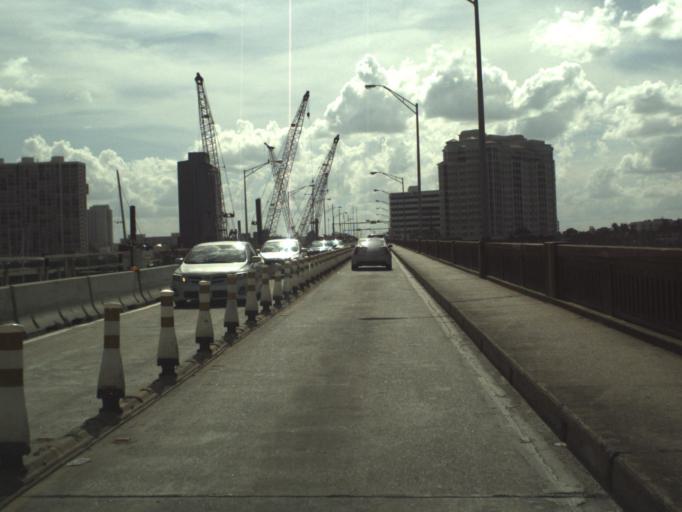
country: US
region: Florida
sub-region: Palm Beach County
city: West Palm Beach
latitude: 26.7182
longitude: -80.0440
